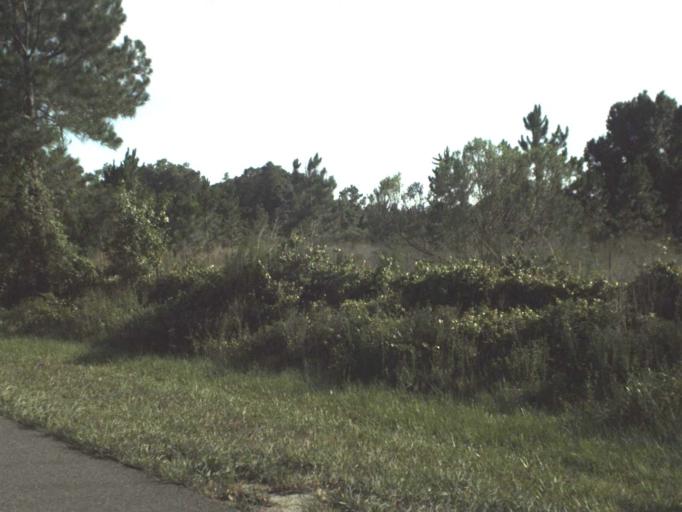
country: US
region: Florida
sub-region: Lake County
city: Clermont
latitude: 28.3896
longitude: -81.8254
